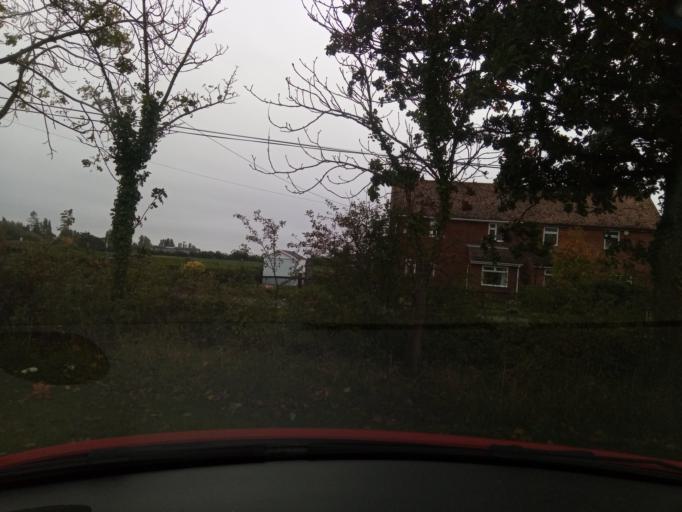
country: GB
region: England
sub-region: Essex
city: West Mersea
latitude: 51.7907
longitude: 0.9687
